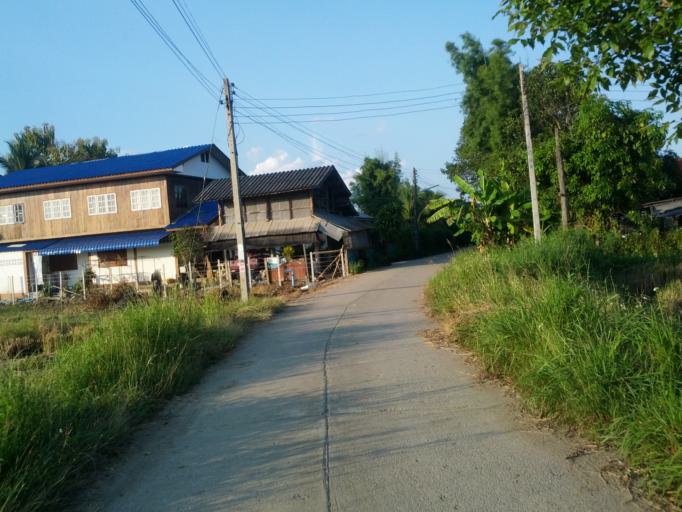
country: TH
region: Chiang Mai
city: San Kamphaeng
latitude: 18.7498
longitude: 99.0833
